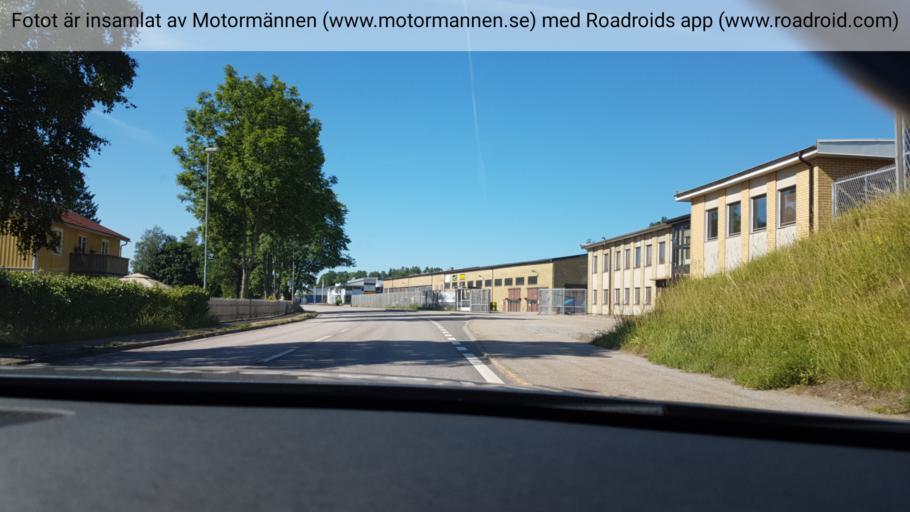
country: SE
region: Vaestra Goetaland
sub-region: Ulricehamns Kommun
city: Ulricehamn
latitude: 57.9255
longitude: 13.4926
